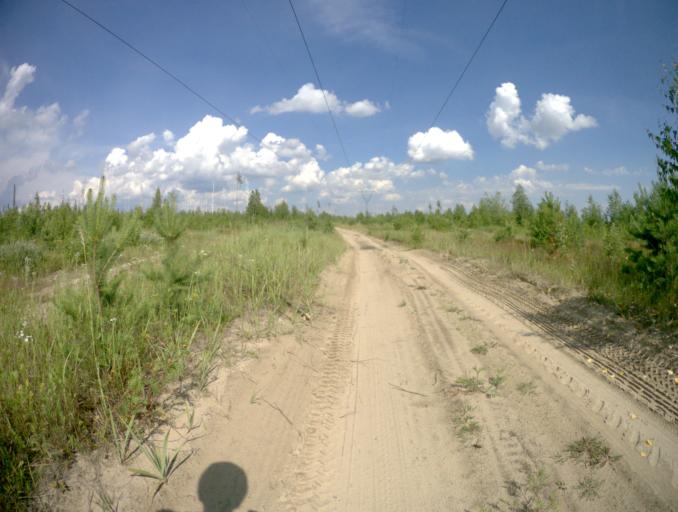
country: RU
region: Ivanovo
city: Talitsy
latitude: 56.5363
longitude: 42.2528
